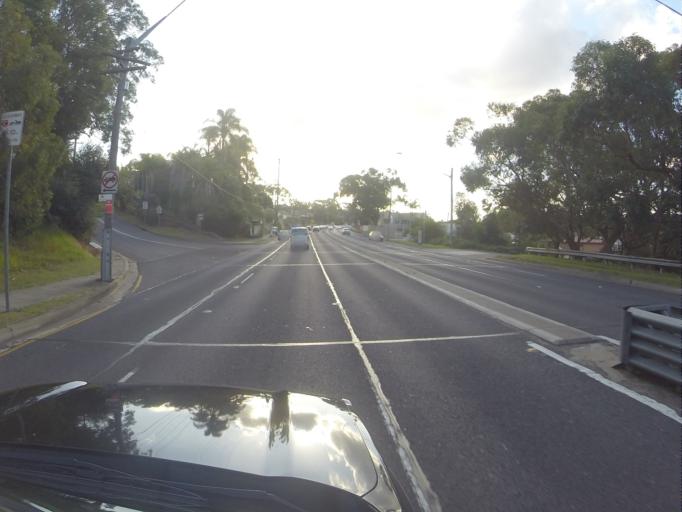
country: AU
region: New South Wales
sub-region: Kogarah
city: Blakehurst
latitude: -33.9944
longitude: 151.1160
